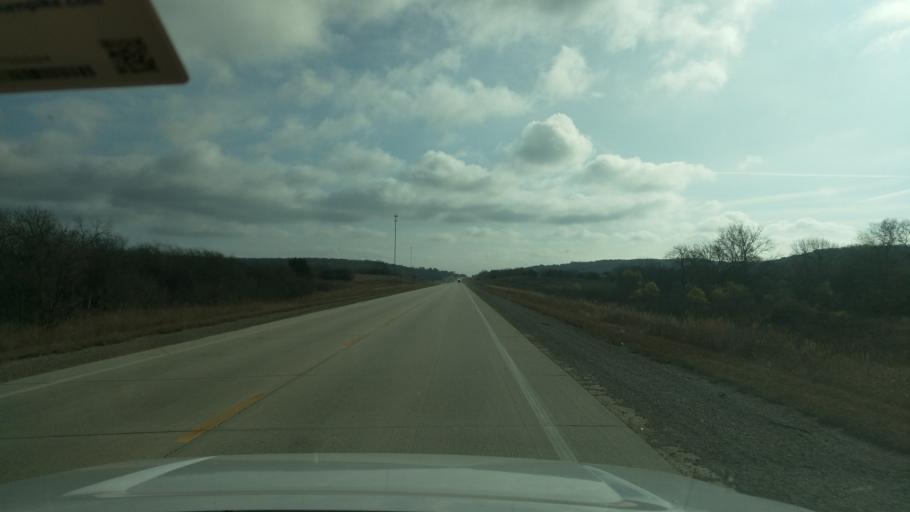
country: US
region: Kansas
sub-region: Chautauqua County
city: Sedan
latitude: 37.0804
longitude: -96.1047
